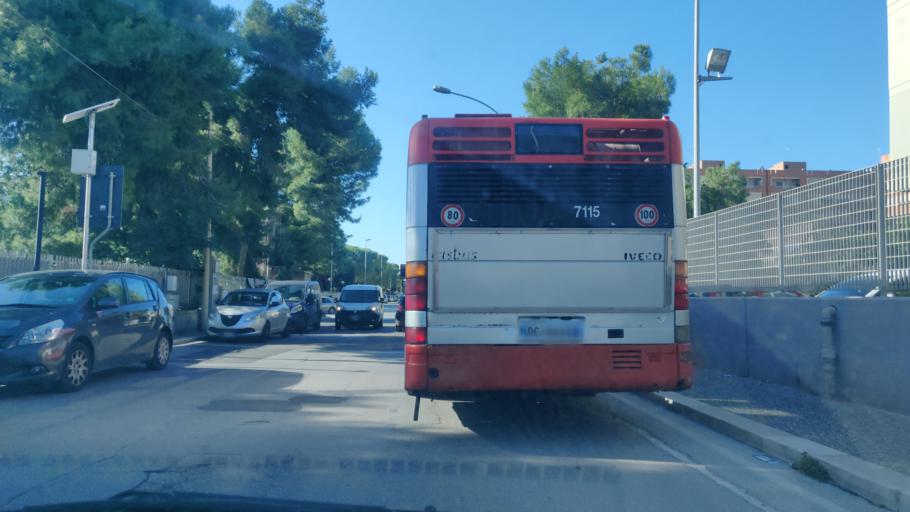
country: IT
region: Apulia
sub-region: Provincia di Bari
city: San Paolo
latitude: 41.1364
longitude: 16.8197
